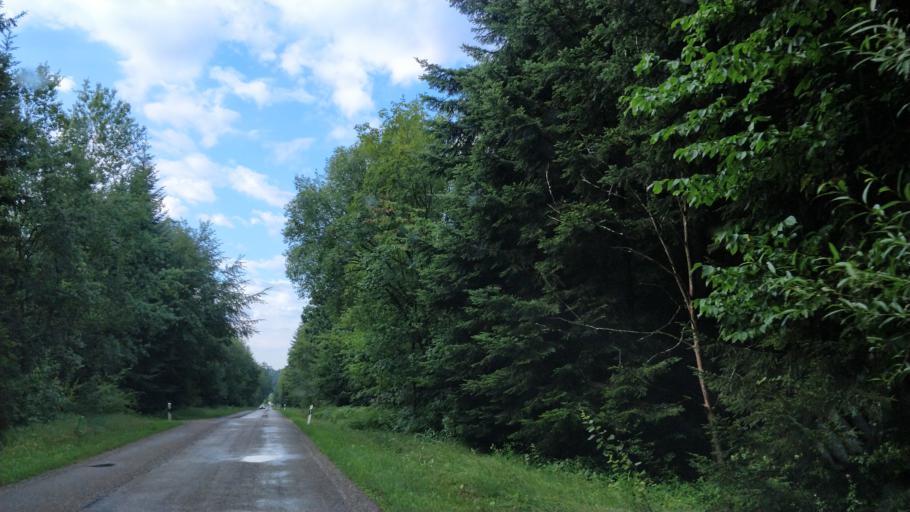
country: DE
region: Baden-Wuerttemberg
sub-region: Regierungsbezirk Stuttgart
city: Fichtenberg
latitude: 48.9661
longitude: 9.6784
